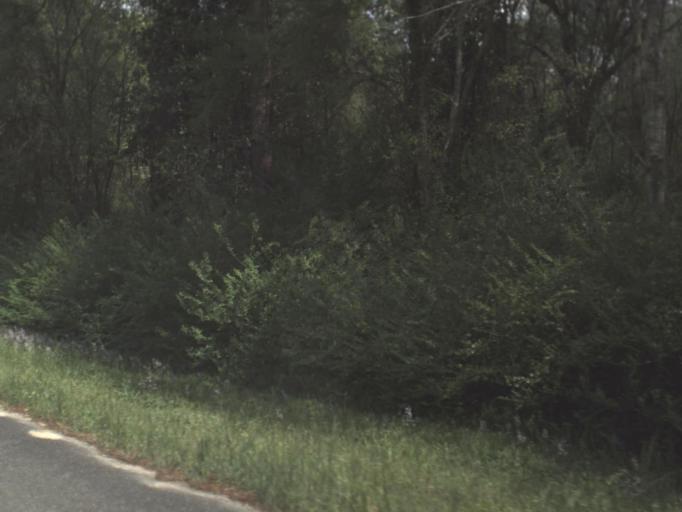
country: US
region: Florida
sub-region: Okaloosa County
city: Crestview
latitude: 30.9302
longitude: -86.6359
